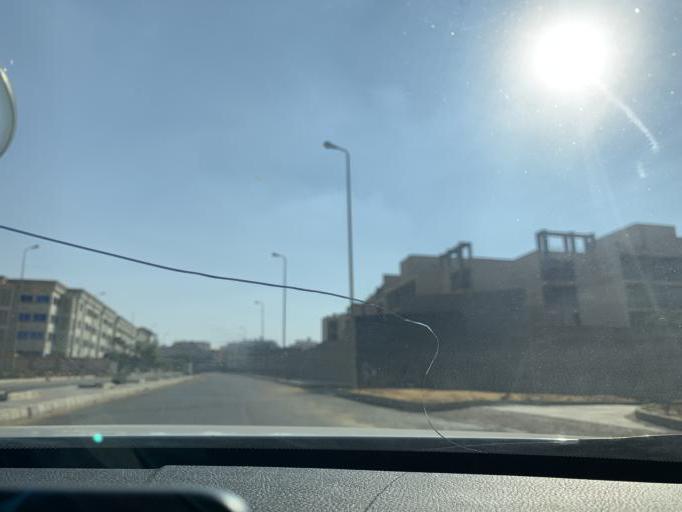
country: EG
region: Muhafazat al Qalyubiyah
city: Al Khankah
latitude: 30.0215
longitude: 31.4792
